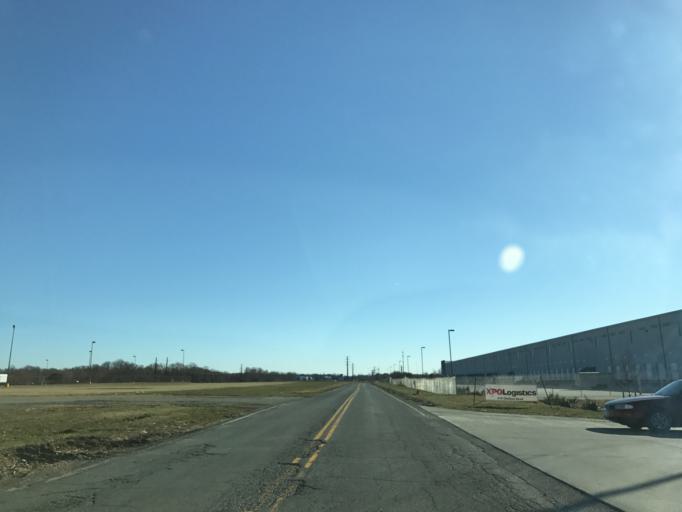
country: US
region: Maryland
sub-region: Harford County
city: Perryman
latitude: 39.4512
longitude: -76.2129
